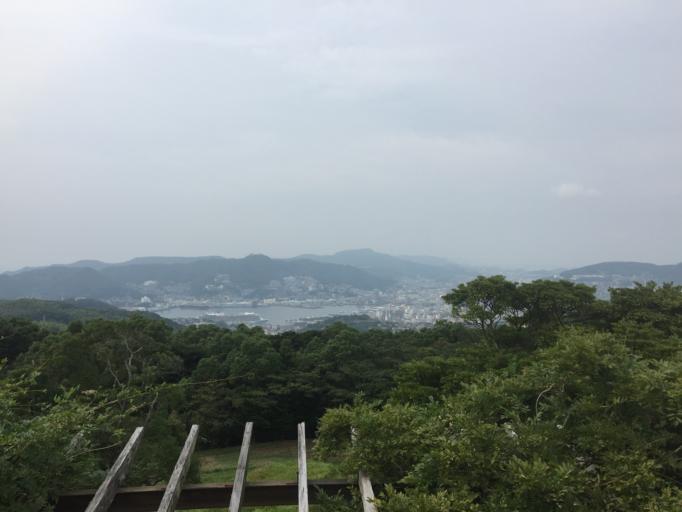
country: JP
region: Nagasaki
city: Nagasaki-shi
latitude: 32.7197
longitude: 129.8886
